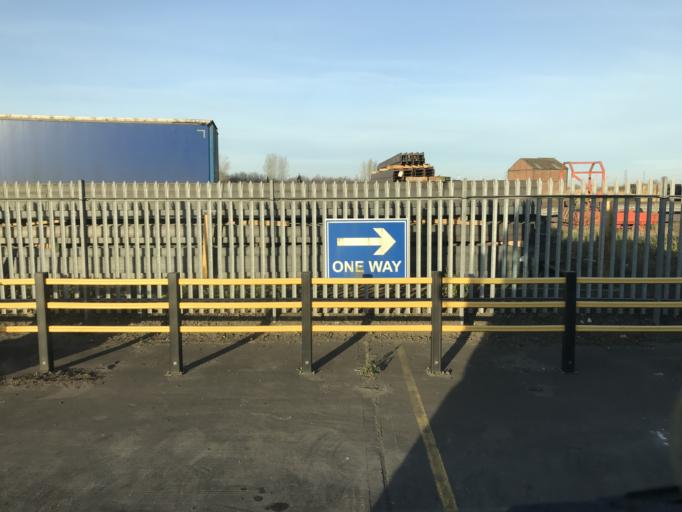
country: GB
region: England
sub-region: North Lincolnshire
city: Burton upon Stather
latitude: 53.6208
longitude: -0.7032
